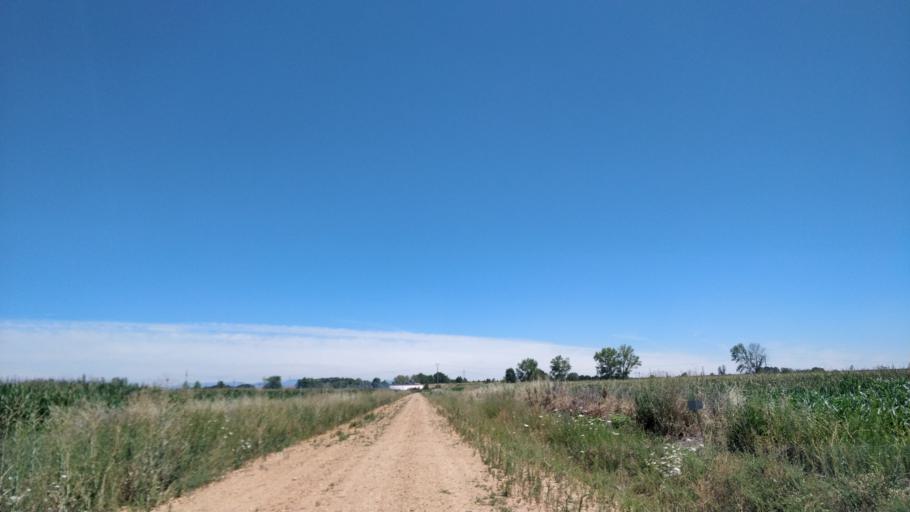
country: ES
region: Castille and Leon
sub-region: Provincia de Leon
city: Bustillo del Paramo
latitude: 42.4720
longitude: -5.8126
